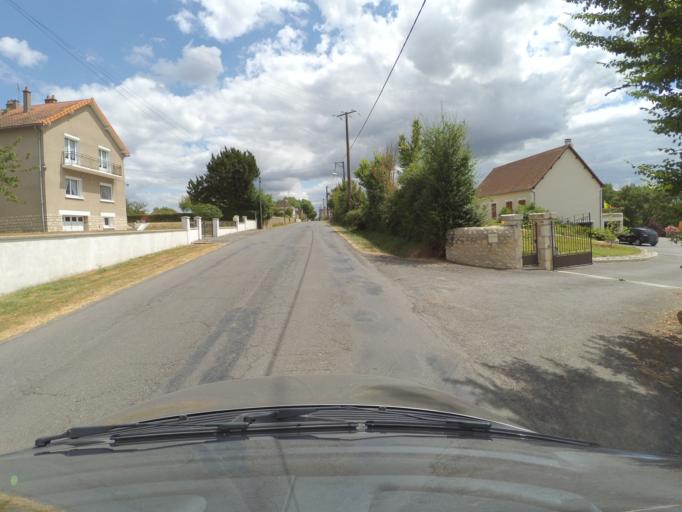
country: FR
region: Centre
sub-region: Departement de l'Indre
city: Belabre
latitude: 46.4645
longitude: 1.0528
